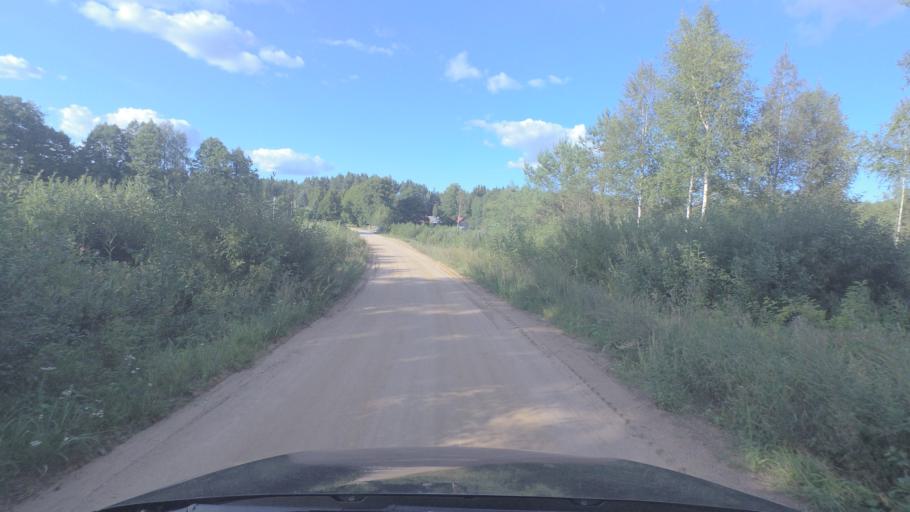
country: LT
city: Pabrade
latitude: 55.1488
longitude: 25.7648
